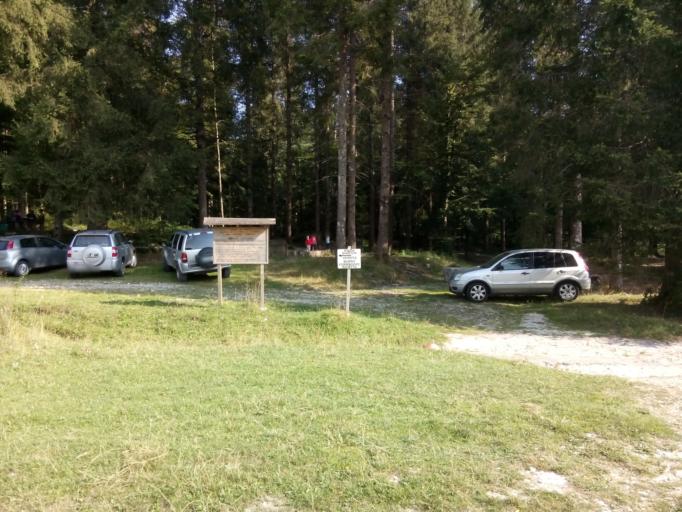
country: IT
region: Veneto
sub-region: Provincia di Vicenza
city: Conco
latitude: 45.8234
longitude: 11.6202
